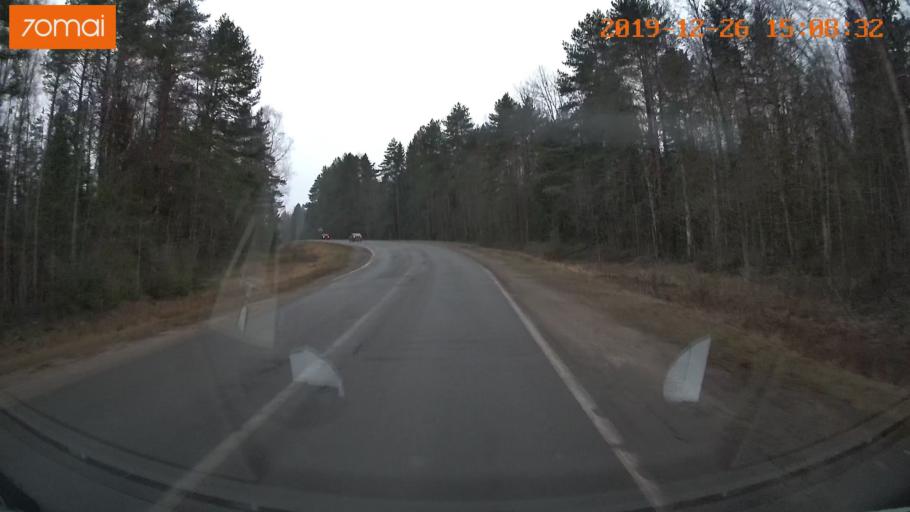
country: RU
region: Jaroslavl
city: Rybinsk
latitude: 58.1588
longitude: 38.8373
